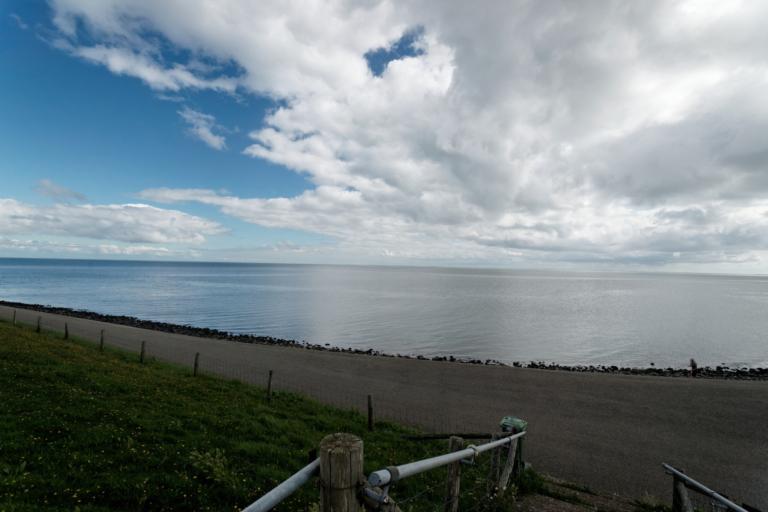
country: NL
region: North Holland
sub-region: Gemeente Texel
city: Den Burg
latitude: 53.0717
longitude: 4.8818
